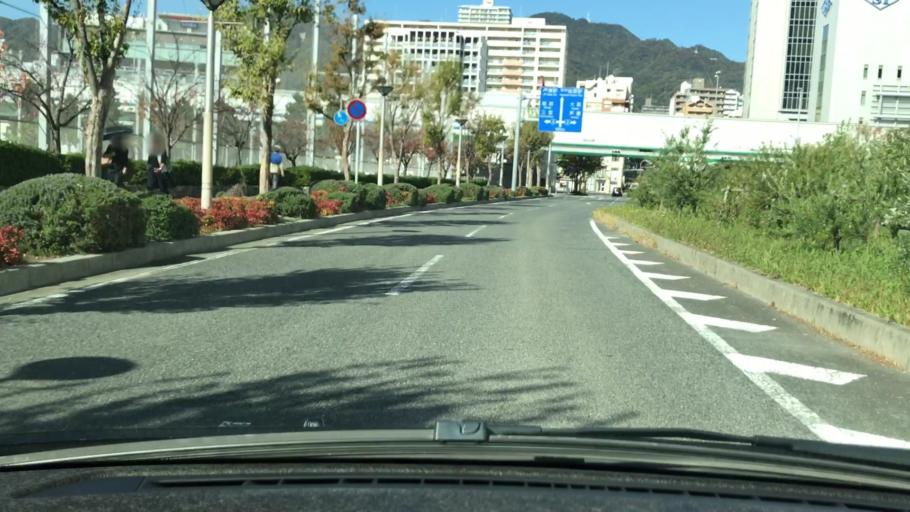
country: JP
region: Hyogo
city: Kobe
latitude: 34.7009
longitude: 135.2179
